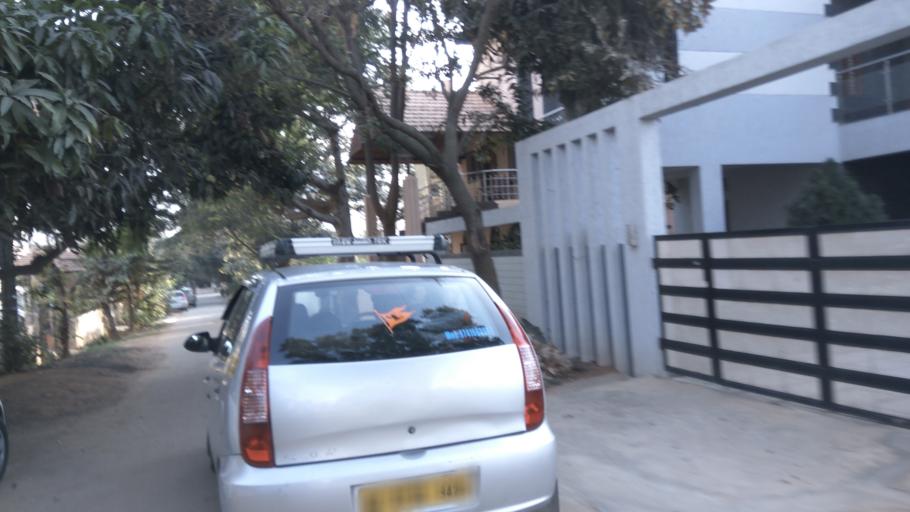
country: IN
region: Karnataka
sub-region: Bangalore Urban
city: Yelahanka
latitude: 13.0670
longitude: 77.6290
